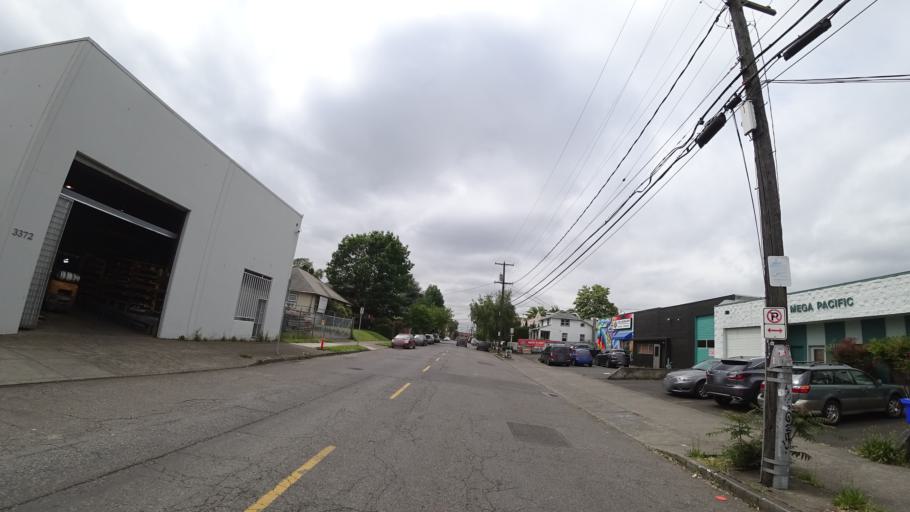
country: US
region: Oregon
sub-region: Multnomah County
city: Portland
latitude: 45.4986
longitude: -122.6447
